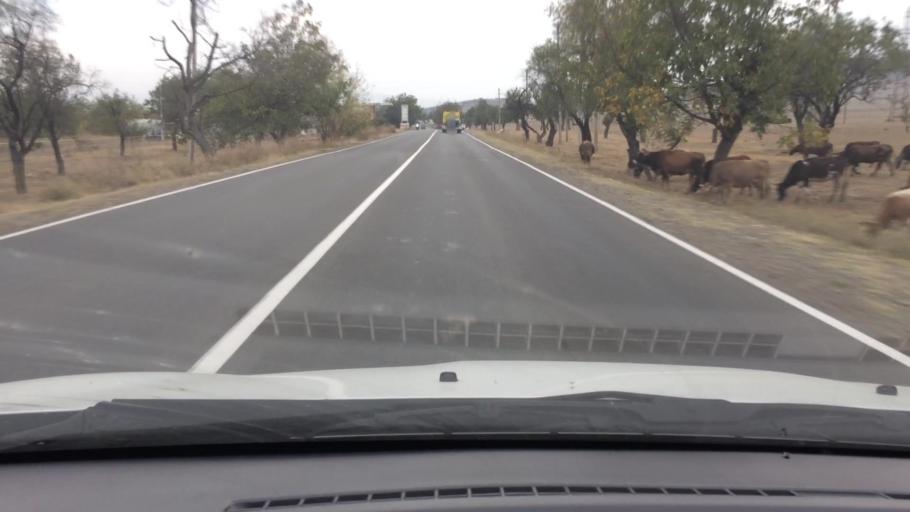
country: GE
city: Naghvarevi
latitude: 41.3839
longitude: 44.8302
